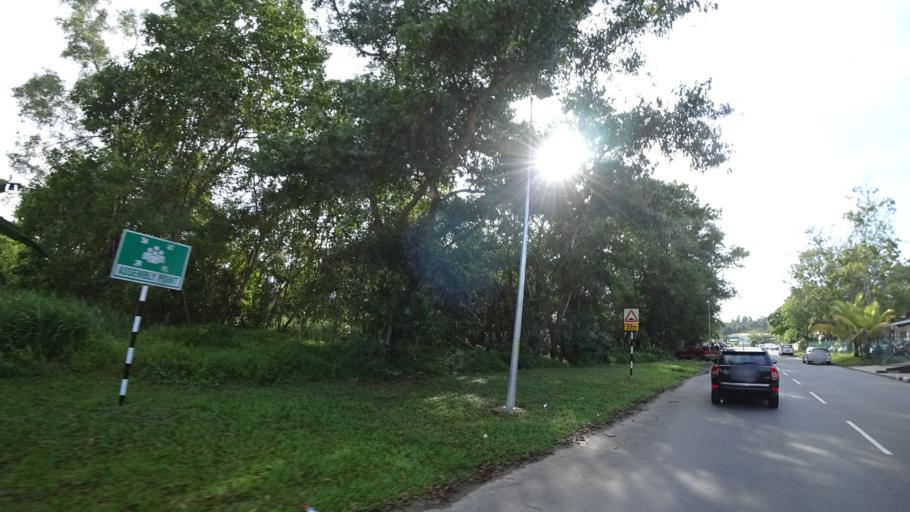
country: BN
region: Brunei and Muara
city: Bandar Seri Begawan
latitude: 4.8923
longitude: 114.9004
